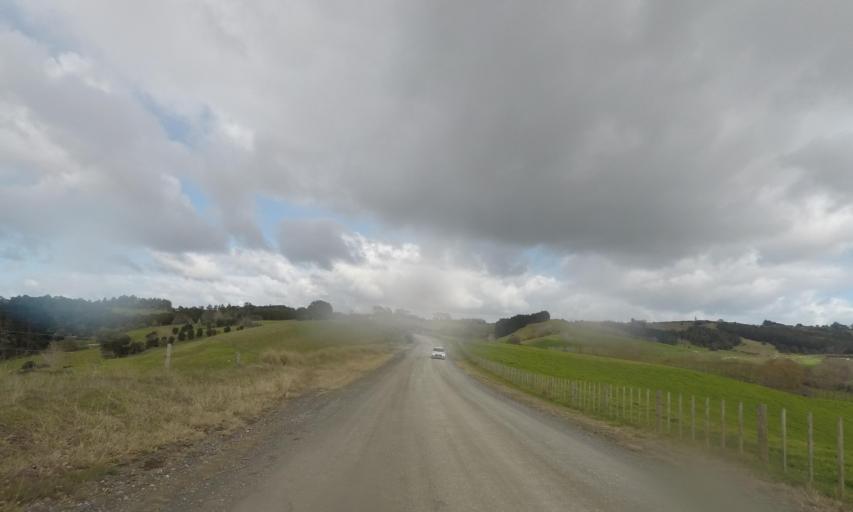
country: NZ
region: Auckland
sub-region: Auckland
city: Wellsford
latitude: -36.1636
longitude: 174.6029
